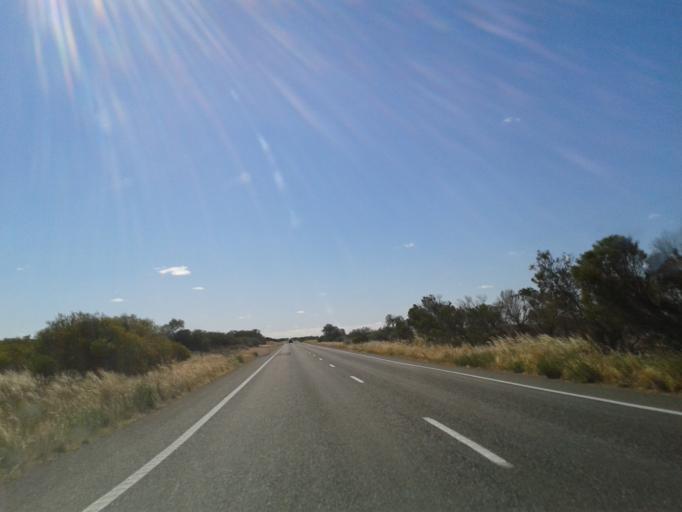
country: AU
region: South Australia
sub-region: Renmark Paringa
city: Renmark
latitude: -34.2744
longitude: 141.2001
